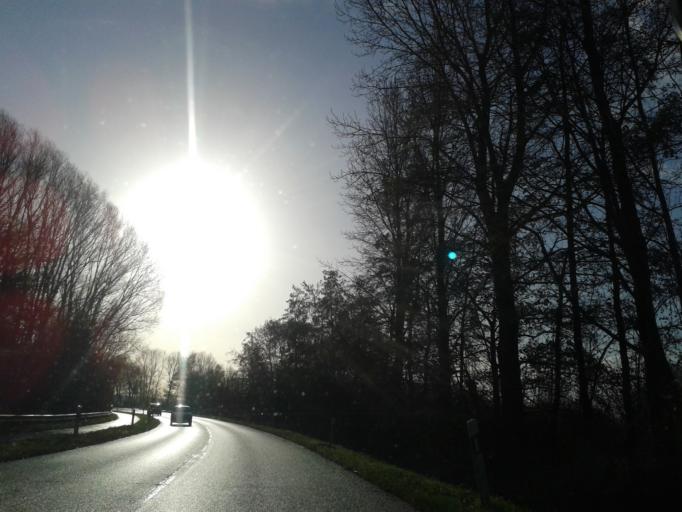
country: DE
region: North Rhine-Westphalia
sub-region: Regierungsbezirk Dusseldorf
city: Xanten
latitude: 51.6861
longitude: 6.4249
